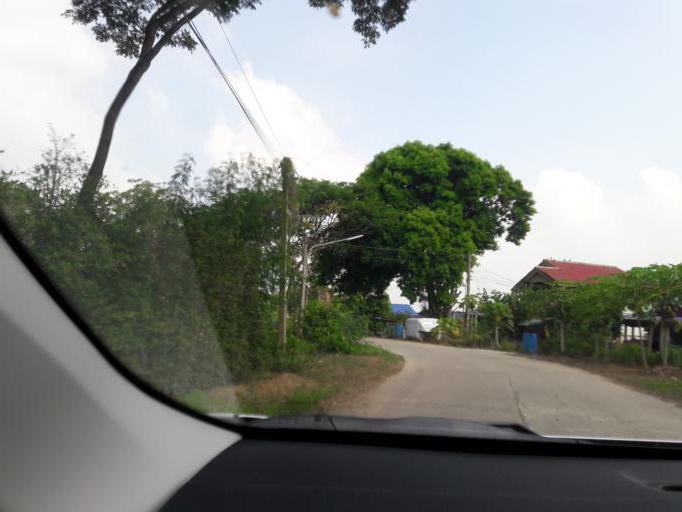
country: TH
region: Ang Thong
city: Ang Thong
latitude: 14.5491
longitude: 100.4372
